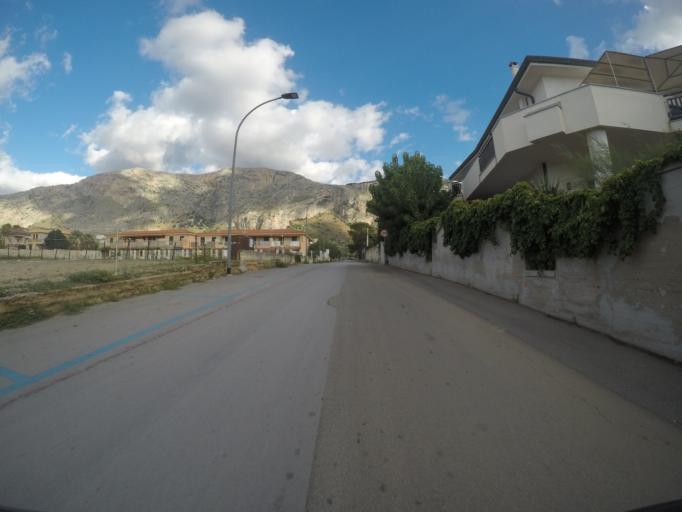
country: IT
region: Sicily
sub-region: Palermo
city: Isola delle Femmine
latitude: 38.1862
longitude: 13.2393
